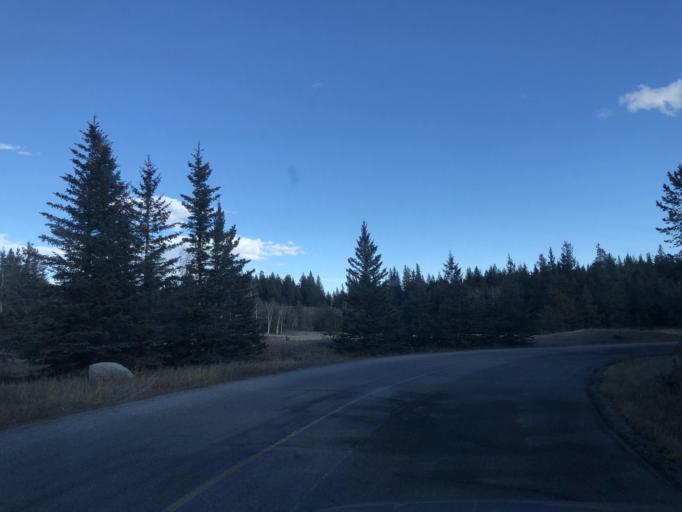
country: CA
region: Alberta
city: Canmore
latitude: 51.0805
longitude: -115.0802
